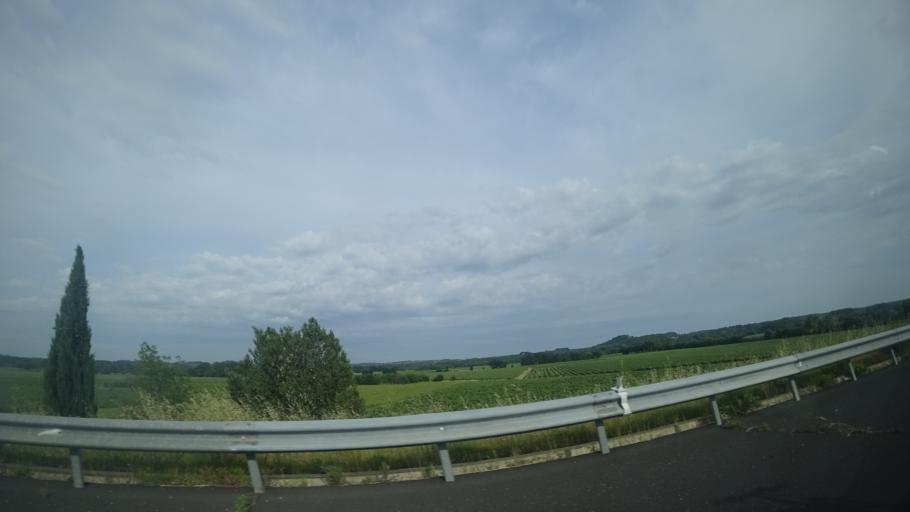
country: FR
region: Languedoc-Roussillon
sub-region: Departement de l'Herault
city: Lezignan-la-Cebe
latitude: 43.4927
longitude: 3.4461
